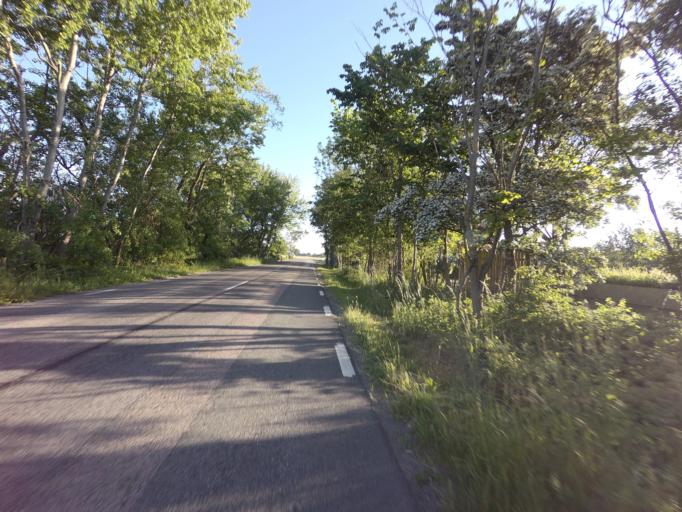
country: SE
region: Skane
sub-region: Helsingborg
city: Odakra
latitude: 56.1975
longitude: 12.6746
